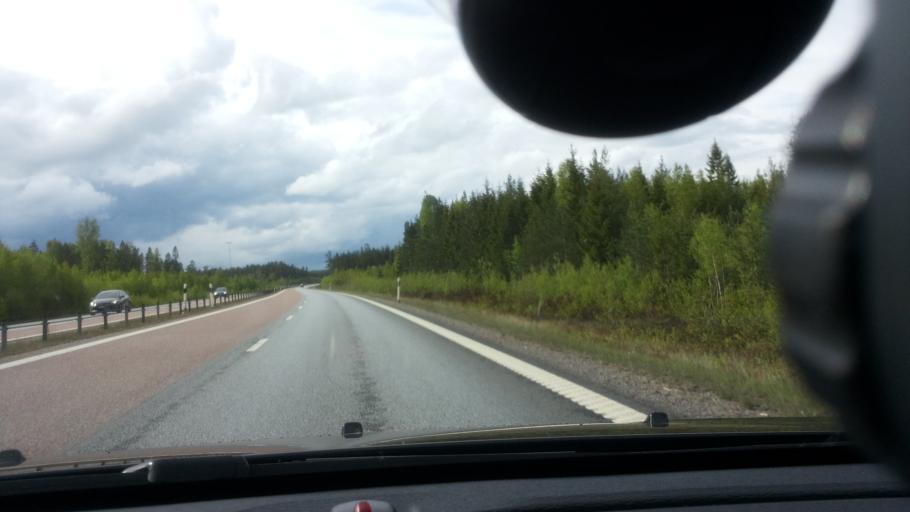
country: SE
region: Gaevleborg
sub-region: Soderhamns Kommun
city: Soderhamn
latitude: 61.4110
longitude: 16.9926
